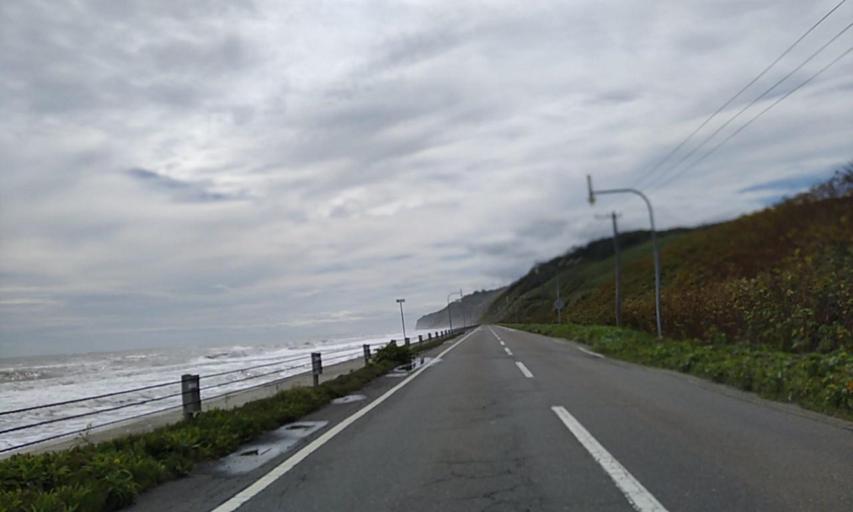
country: JP
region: Hokkaido
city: Obihiro
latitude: 42.7824
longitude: 143.7864
